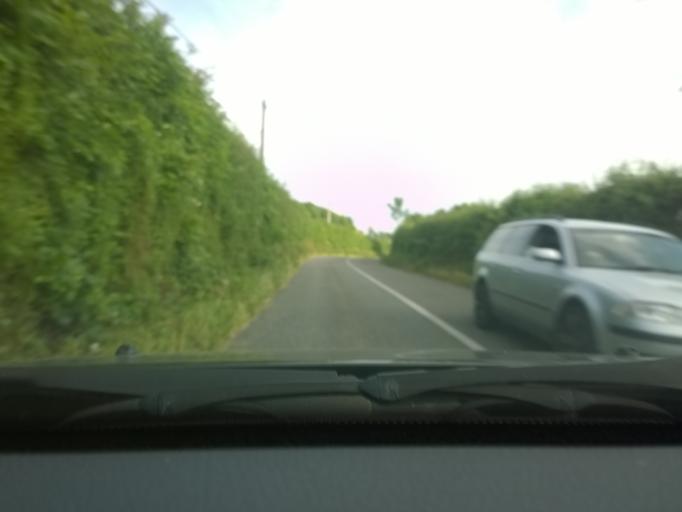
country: IE
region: Leinster
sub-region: Kildare
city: Cherryville
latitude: 53.1918
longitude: -6.9494
